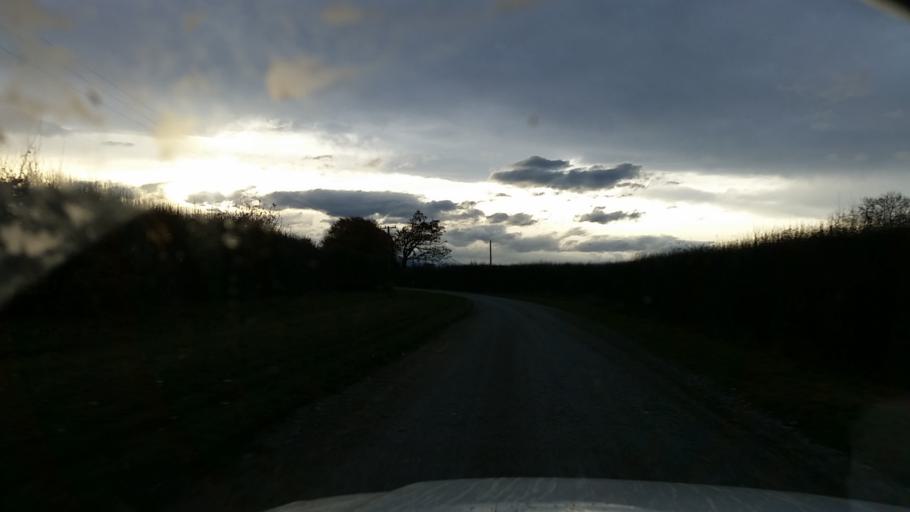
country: NZ
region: Canterbury
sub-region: Ashburton District
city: Ashburton
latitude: -43.8364
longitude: 171.6543
